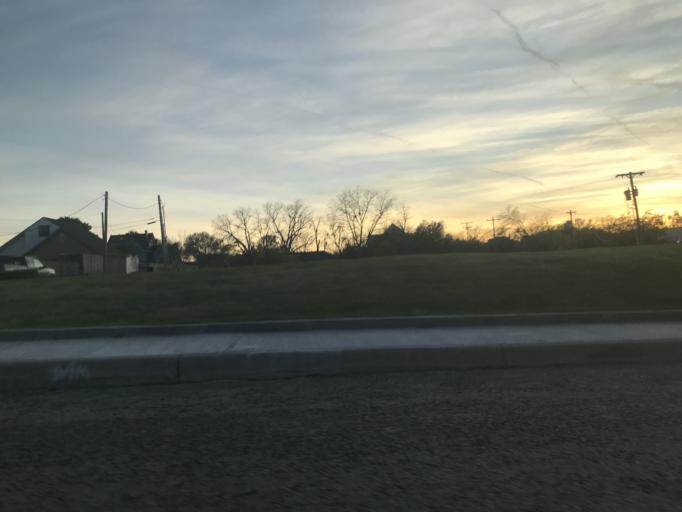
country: US
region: Texas
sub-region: Tom Green County
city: San Angelo
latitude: 31.4585
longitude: -100.4514
